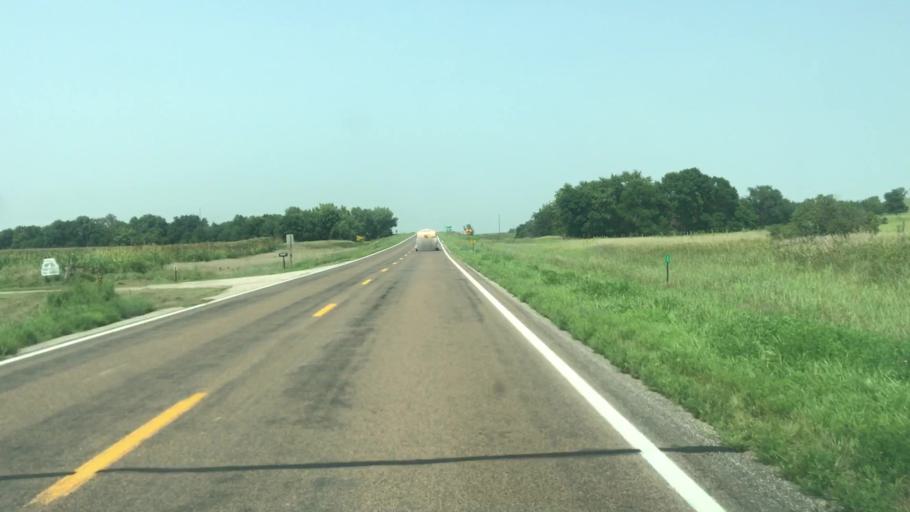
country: US
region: Nebraska
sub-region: Sherman County
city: Loup City
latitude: 41.2572
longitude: -98.9389
